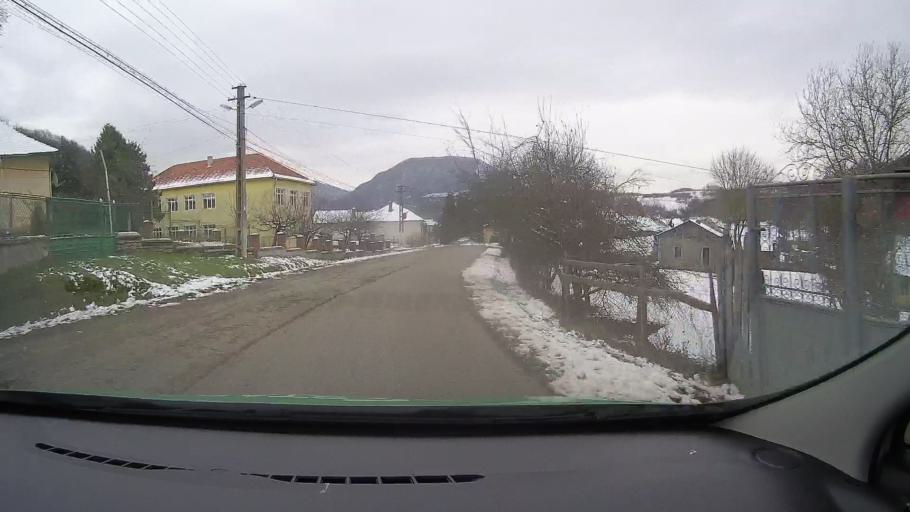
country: RO
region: Hunedoara
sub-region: Comuna Balsa
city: Balsa
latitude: 46.0292
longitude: 23.0987
